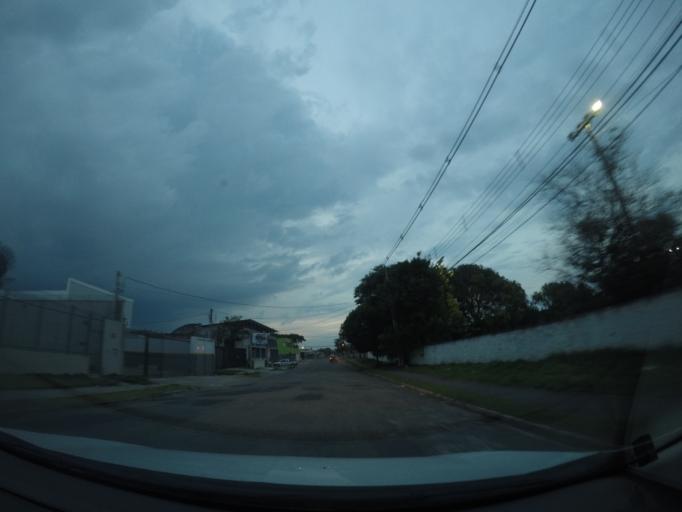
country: BR
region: Parana
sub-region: Sao Jose Dos Pinhais
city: Sao Jose dos Pinhais
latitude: -25.4940
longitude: -49.2329
